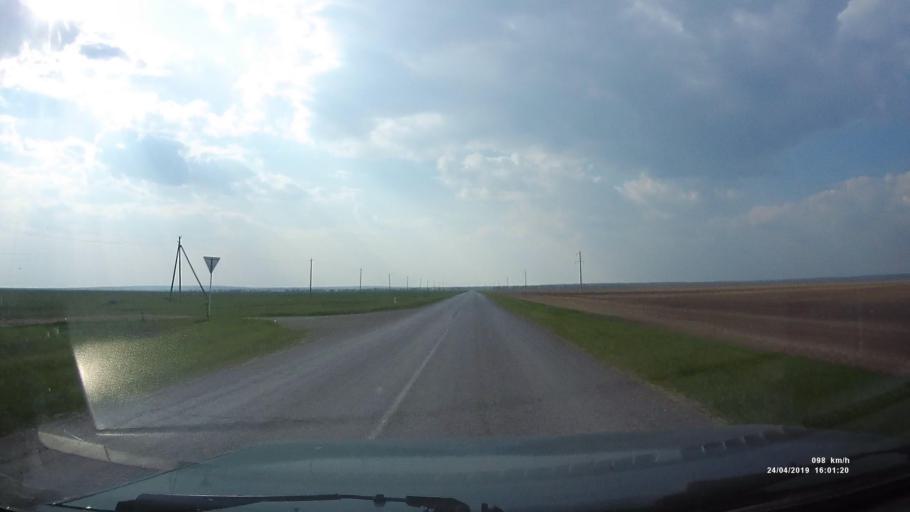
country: RU
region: Rostov
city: Sovetskoye
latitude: 46.6415
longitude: 42.4364
